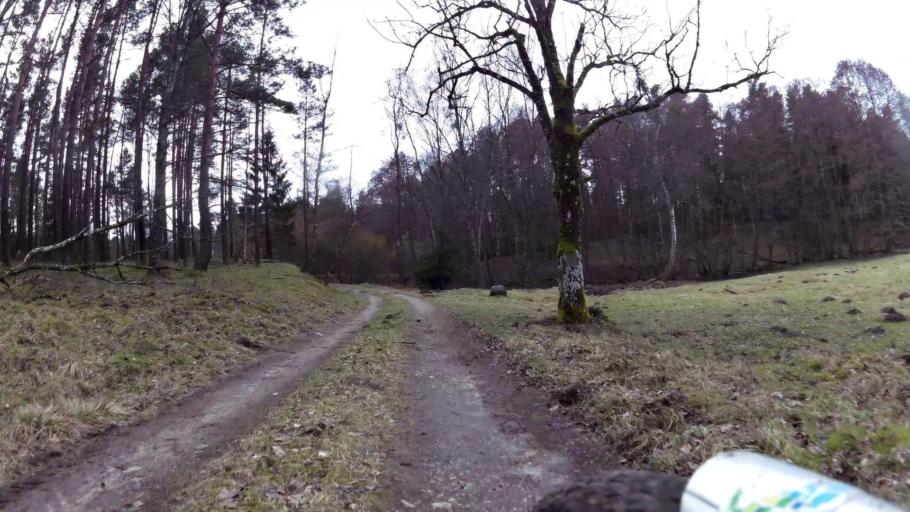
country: PL
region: Pomeranian Voivodeship
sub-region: Powiat bytowski
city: Trzebielino
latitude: 54.1485
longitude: 17.1588
